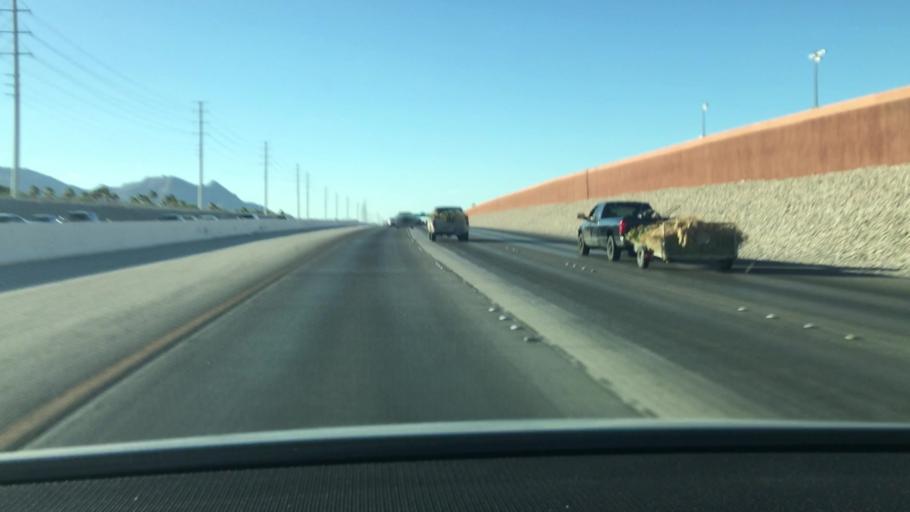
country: US
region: Nevada
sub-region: Clark County
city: Summerlin South
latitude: 36.1347
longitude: -115.3362
